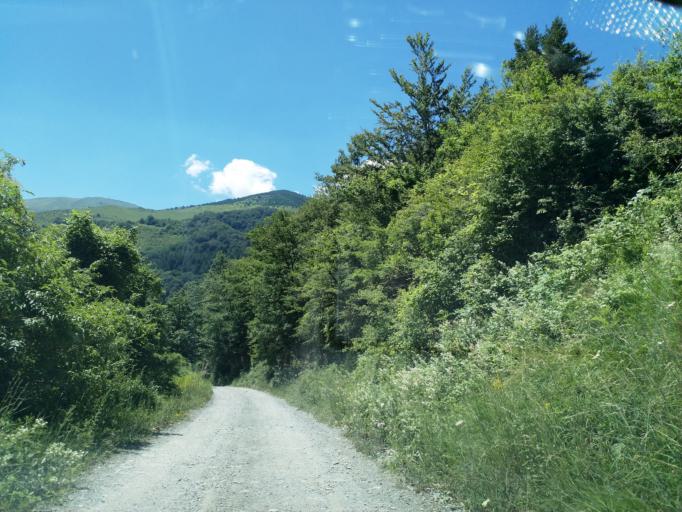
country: XK
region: Mitrovica
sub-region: Komuna e Leposaviqit
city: Leposaviq
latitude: 43.2774
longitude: 20.8749
